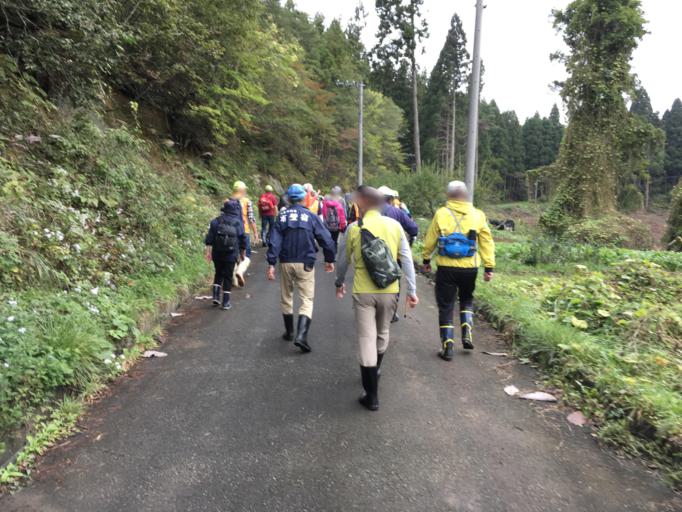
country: JP
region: Iwate
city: Ichinoseki
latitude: 38.8715
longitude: 141.1273
